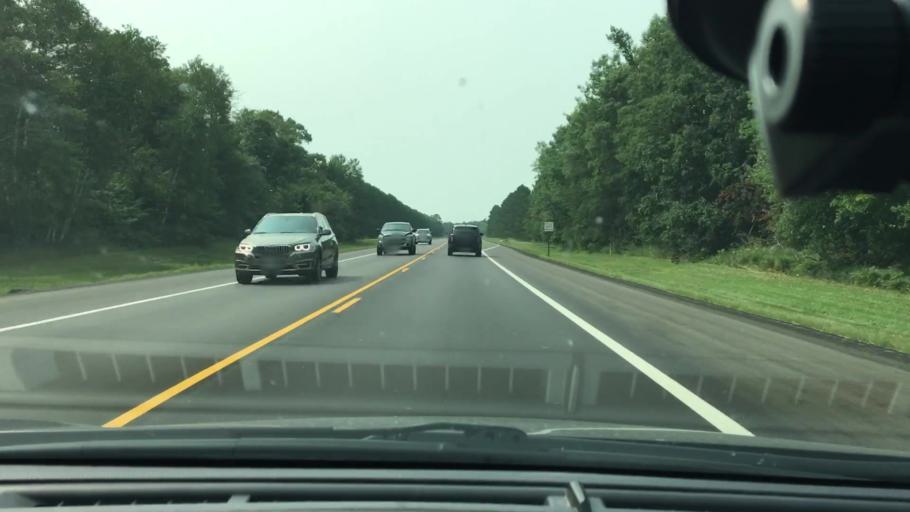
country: US
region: Minnesota
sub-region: Crow Wing County
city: Brainerd
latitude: 46.4332
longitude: -94.1733
